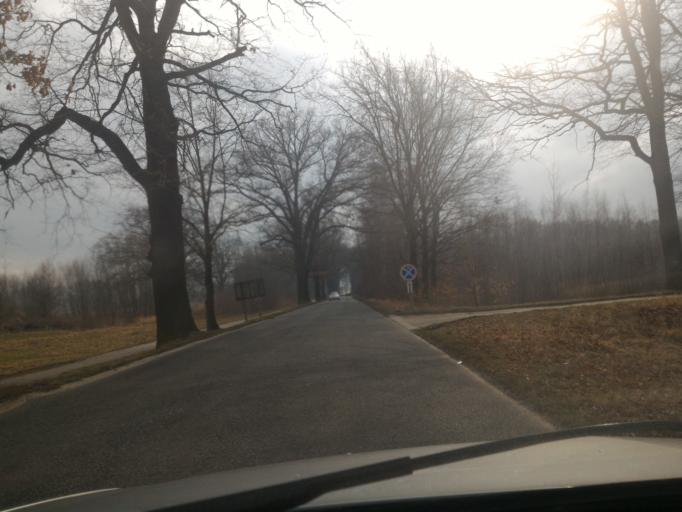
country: CZ
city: Hradek nad Nisou
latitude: 50.8752
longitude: 14.8260
